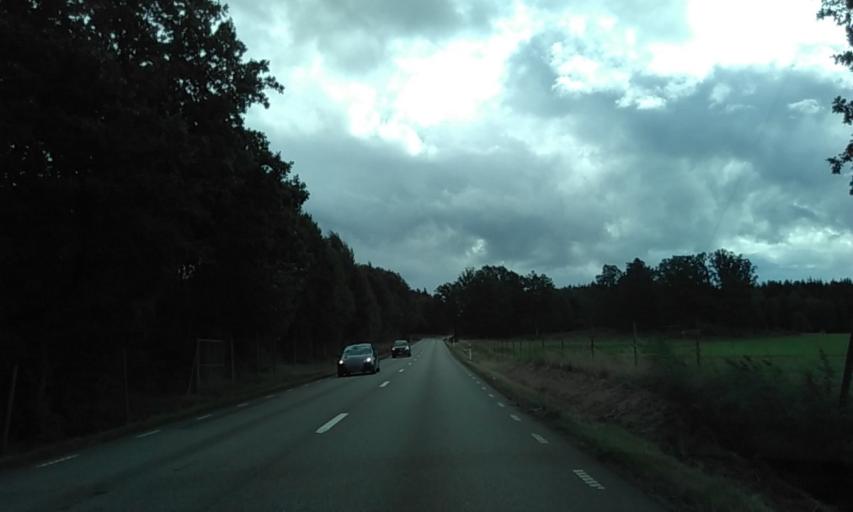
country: SE
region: Vaestra Goetaland
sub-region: Alingsas Kommun
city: Alingsas
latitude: 57.9610
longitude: 12.4470
